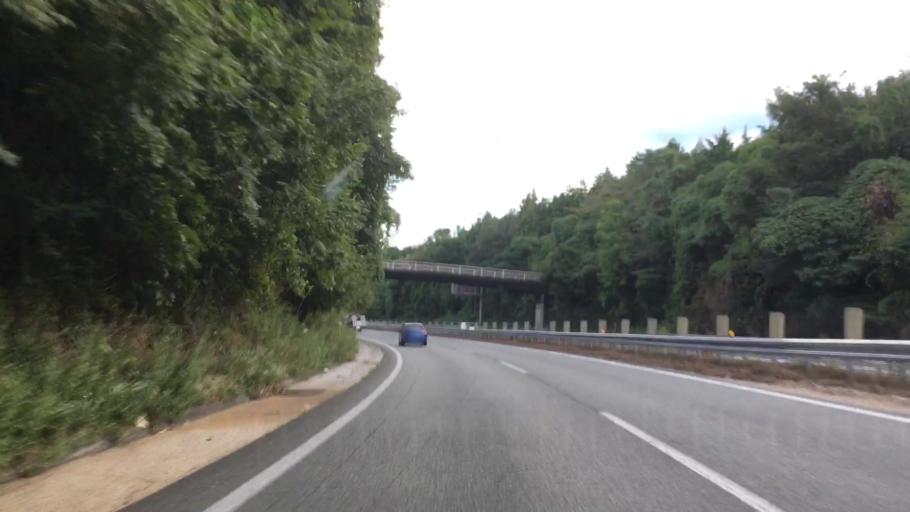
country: JP
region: Yamaguchi
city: Ogori-shimogo
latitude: 34.1678
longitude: 131.2412
